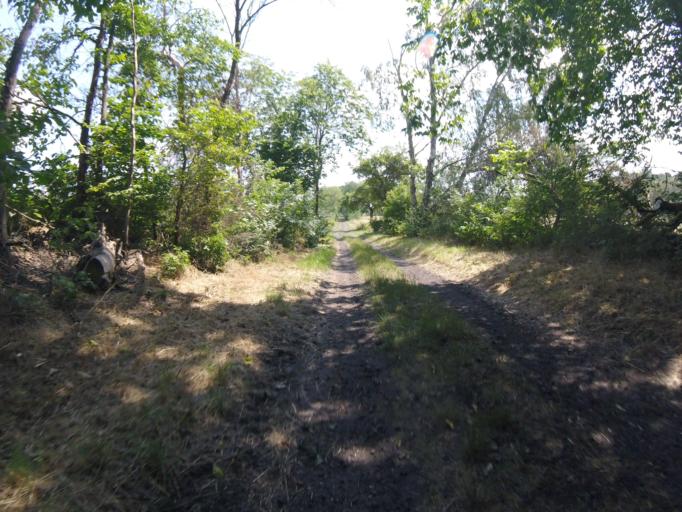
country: DE
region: Brandenburg
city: Bestensee
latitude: 52.2654
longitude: 13.7072
